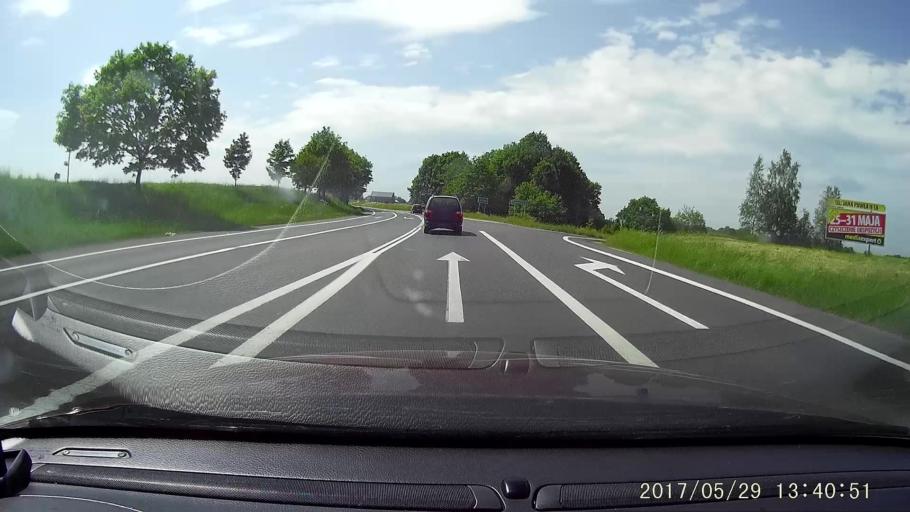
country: PL
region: Lower Silesian Voivodeship
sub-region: Powiat lubanski
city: Luban
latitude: 51.1335
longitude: 15.2681
